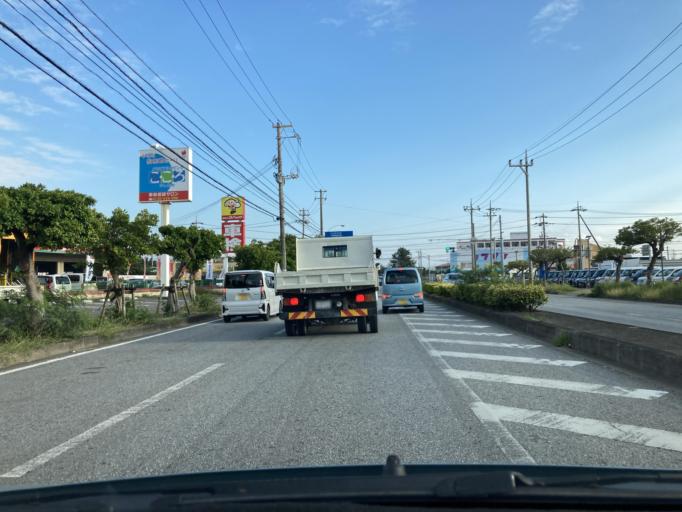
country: JP
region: Okinawa
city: Katsuren-haebaru
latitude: 26.3388
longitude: 127.8463
